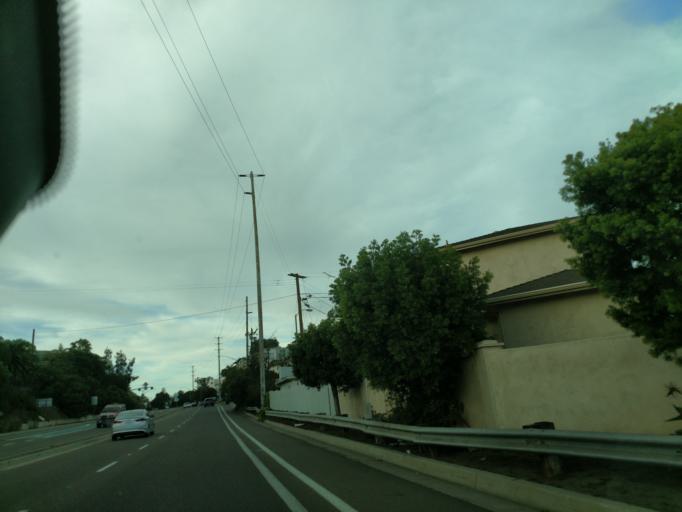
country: US
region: California
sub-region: San Diego County
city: Coronado
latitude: 32.7301
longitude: -117.2278
